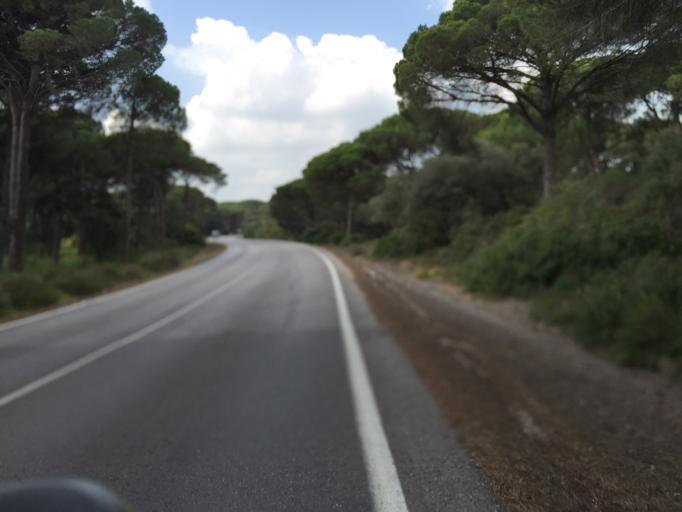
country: ES
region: Andalusia
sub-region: Provincia de Cadiz
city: Vejer de la Frontera
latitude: 36.2927
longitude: -5.9243
